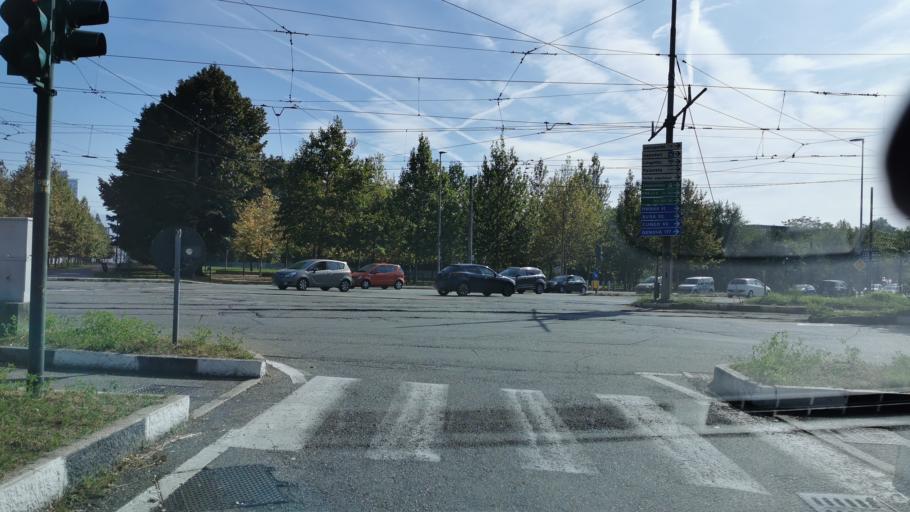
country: IT
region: Piedmont
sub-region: Provincia di Torino
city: Turin
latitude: 45.0918
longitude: 7.6625
